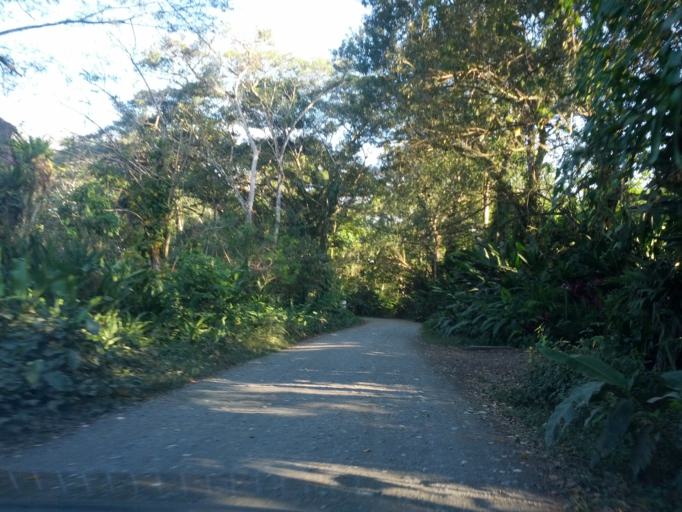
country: CR
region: Puntarenas
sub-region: Canton de Golfito
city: Golfito
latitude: 8.5094
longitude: -83.2942
